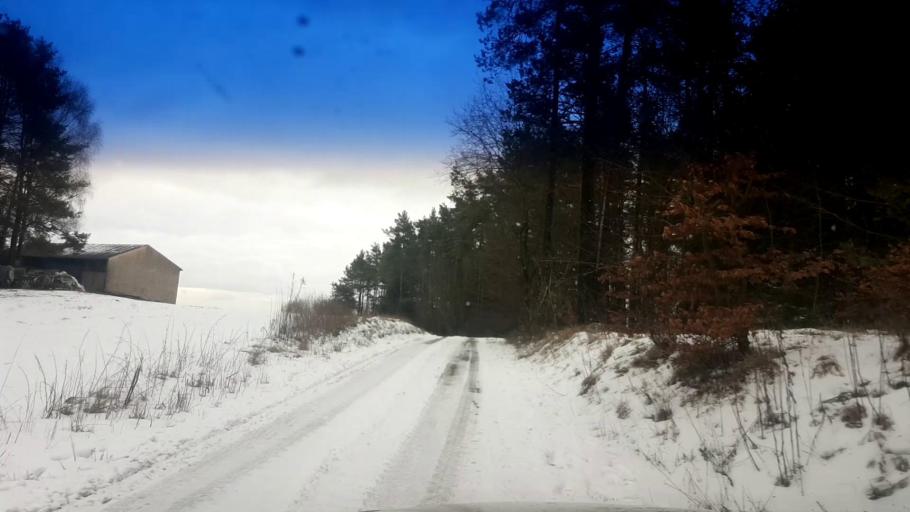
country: DE
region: Bavaria
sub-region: Upper Franconia
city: Wattendorf
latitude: 50.0067
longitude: 11.1249
